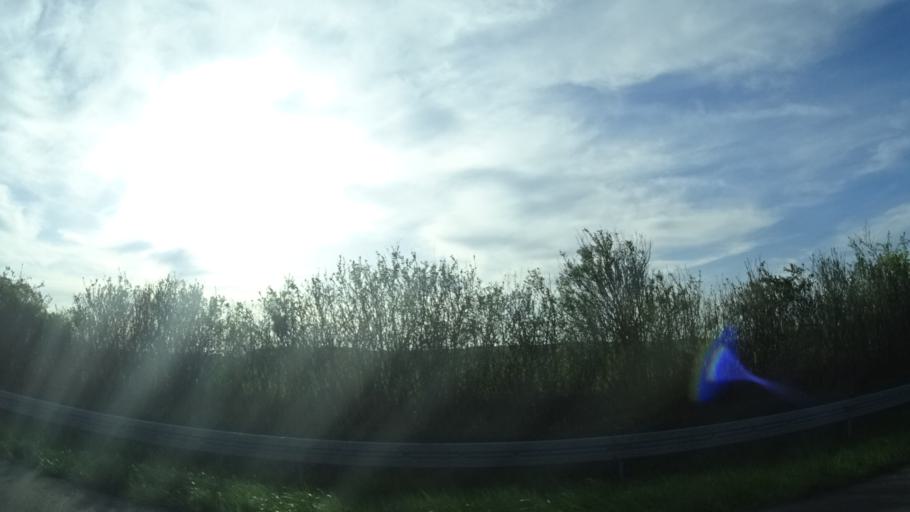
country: DE
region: Baden-Wuerttemberg
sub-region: Regierungsbezirk Stuttgart
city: Grossrinderfeld
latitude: 49.6429
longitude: 9.7332
